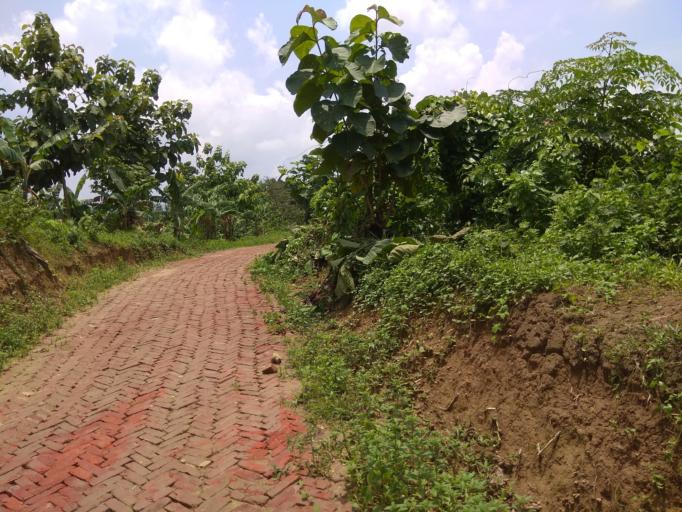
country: BD
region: Chittagong
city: Manikchari
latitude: 22.8854
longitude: 91.9250
